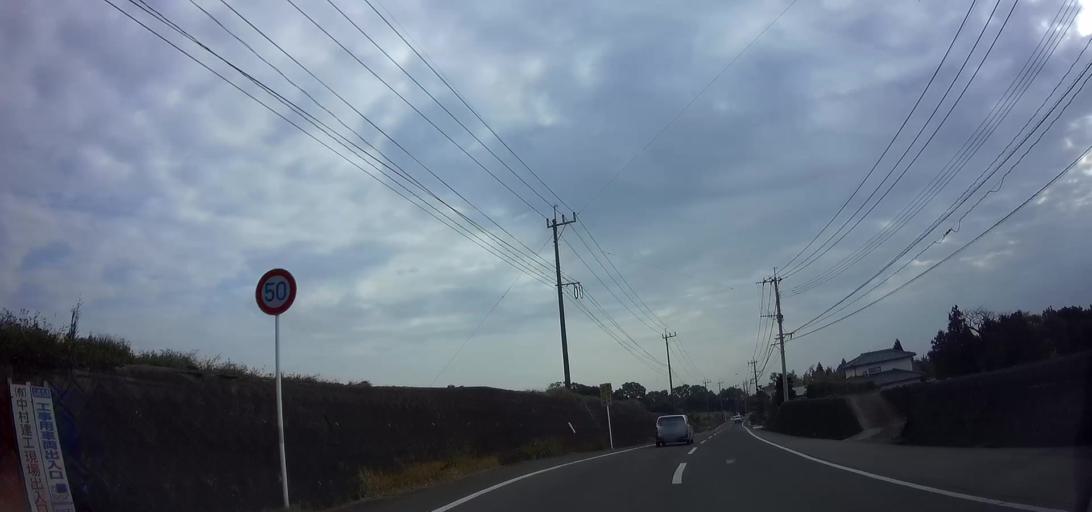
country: JP
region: Nagasaki
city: Shimabara
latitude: 32.6926
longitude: 130.2996
